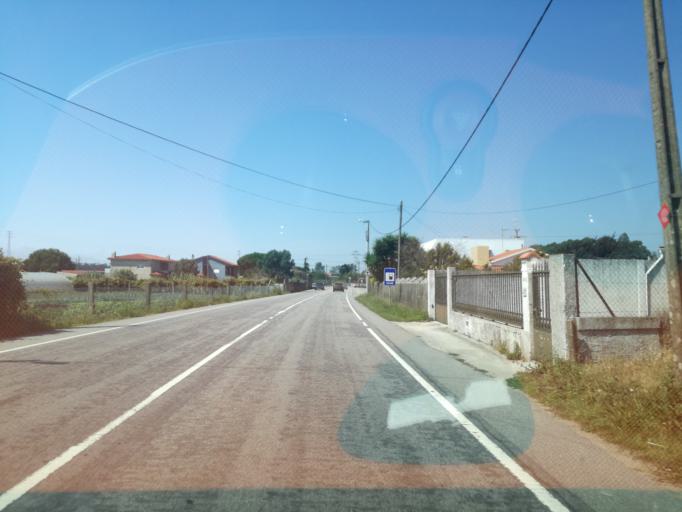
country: PT
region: Braga
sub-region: Esposende
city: Apulia
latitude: 41.4891
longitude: -8.7525
